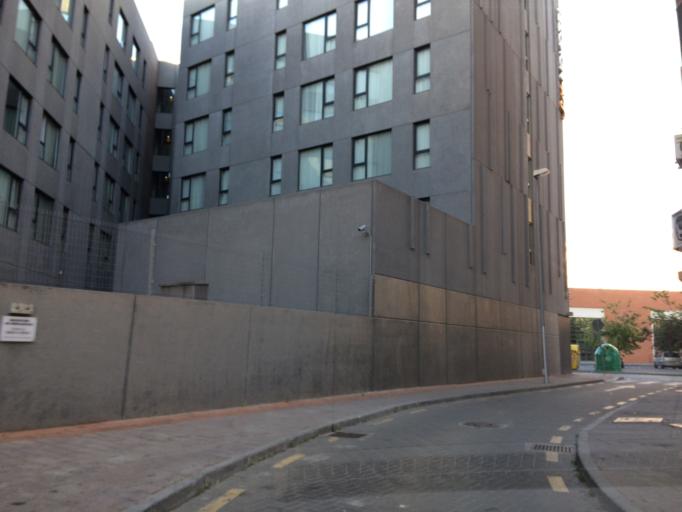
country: ES
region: Andalusia
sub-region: Provincia de Malaga
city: Malaga
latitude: 36.7184
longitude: -4.4277
